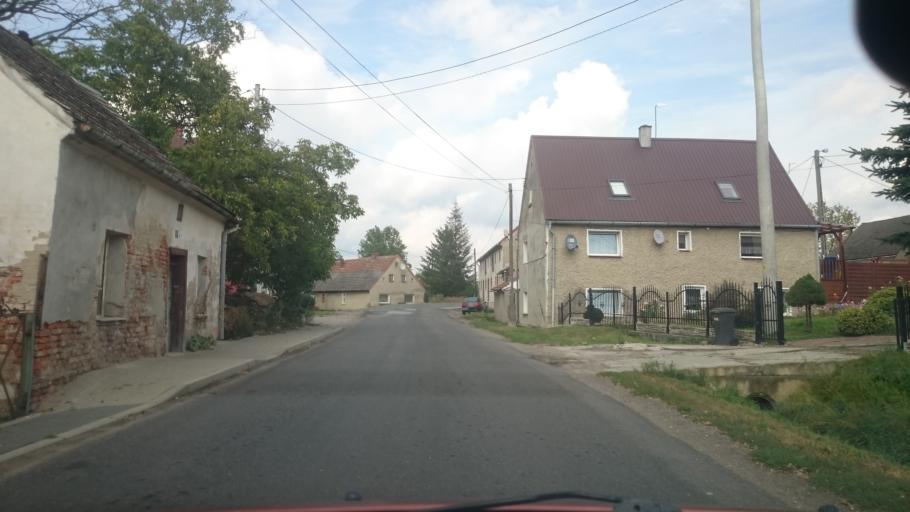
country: PL
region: Opole Voivodeship
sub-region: Powiat nyski
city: Otmuchow
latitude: 50.4999
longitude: 17.2202
